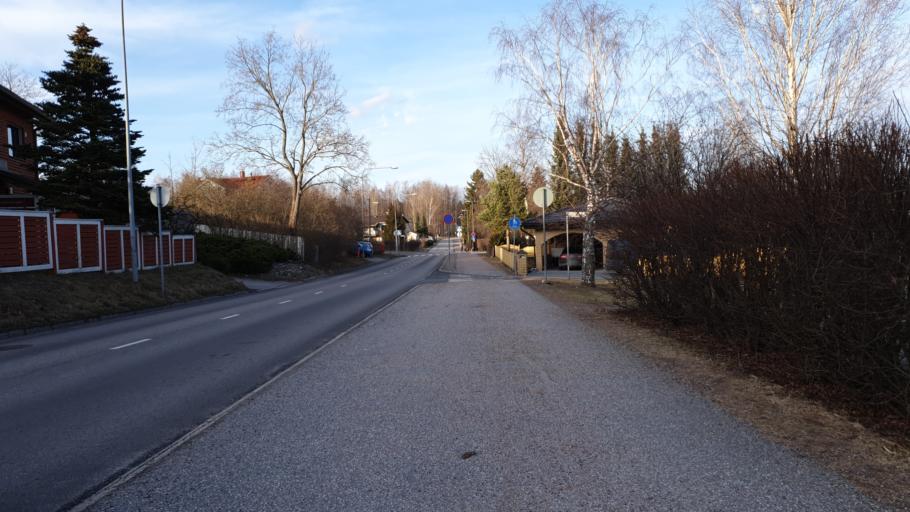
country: FI
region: Uusimaa
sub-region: Helsinki
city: Vantaa
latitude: 60.3104
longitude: 25.0068
